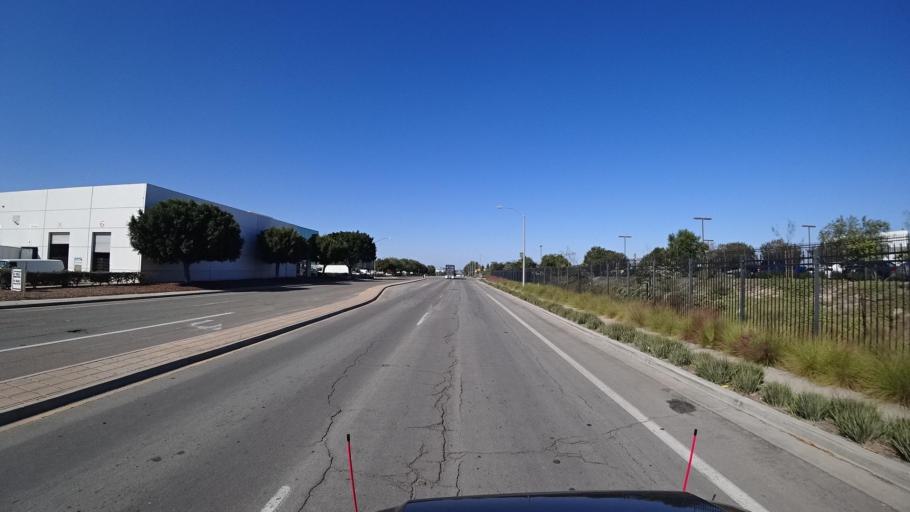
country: MX
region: Baja California
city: Tijuana
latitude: 32.5603
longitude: -116.9348
